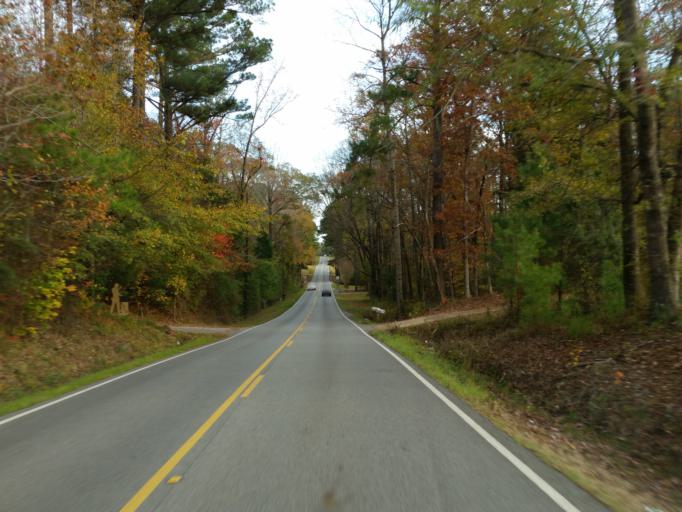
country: US
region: Mississippi
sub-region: Lauderdale County
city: Marion
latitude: 32.4089
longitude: -88.6070
